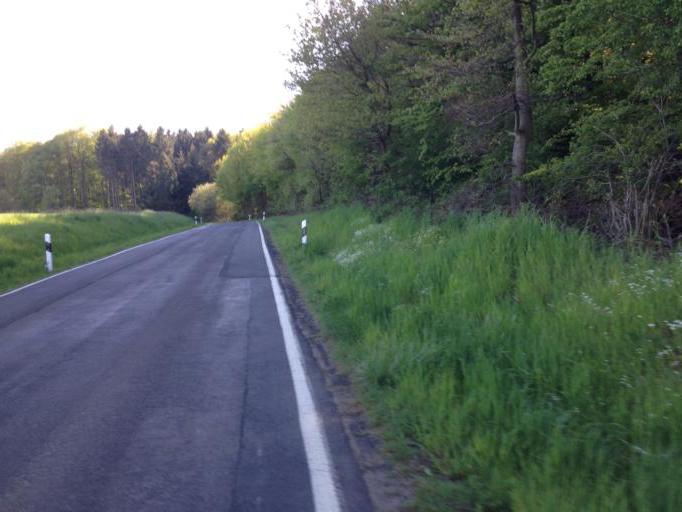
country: DE
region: Hesse
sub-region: Regierungsbezirk Giessen
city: Grossen Buseck
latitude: 50.5724
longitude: 8.7980
